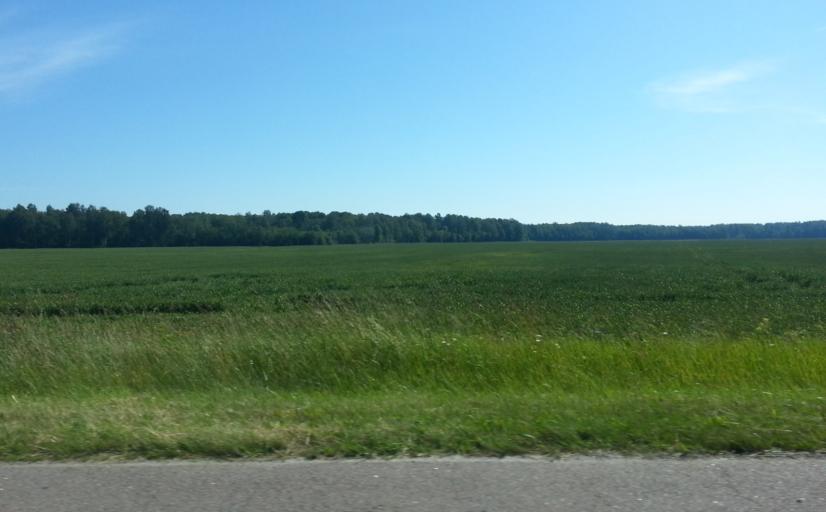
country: LT
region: Vilnius County
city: Ukmerge
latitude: 55.3365
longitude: 24.7618
